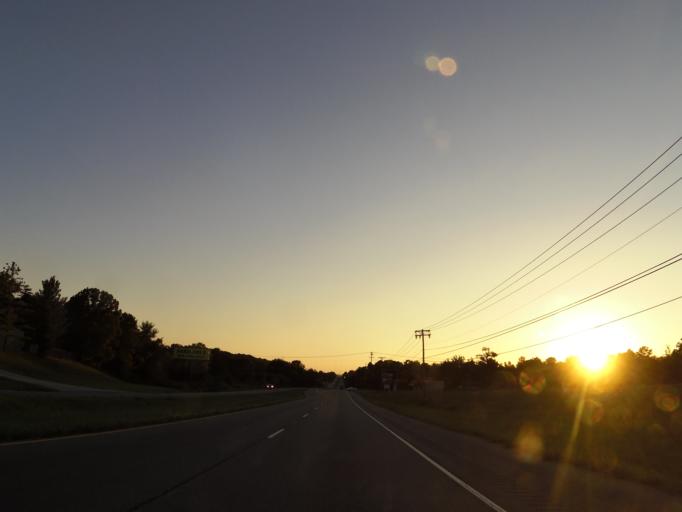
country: US
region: Tennessee
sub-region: Knox County
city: Mascot
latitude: 36.0225
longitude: -83.7671
